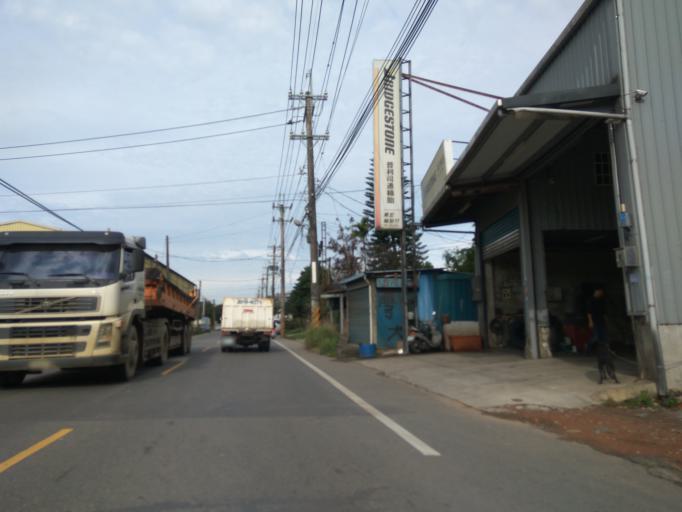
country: TW
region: Taiwan
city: Daxi
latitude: 24.9385
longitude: 121.1616
